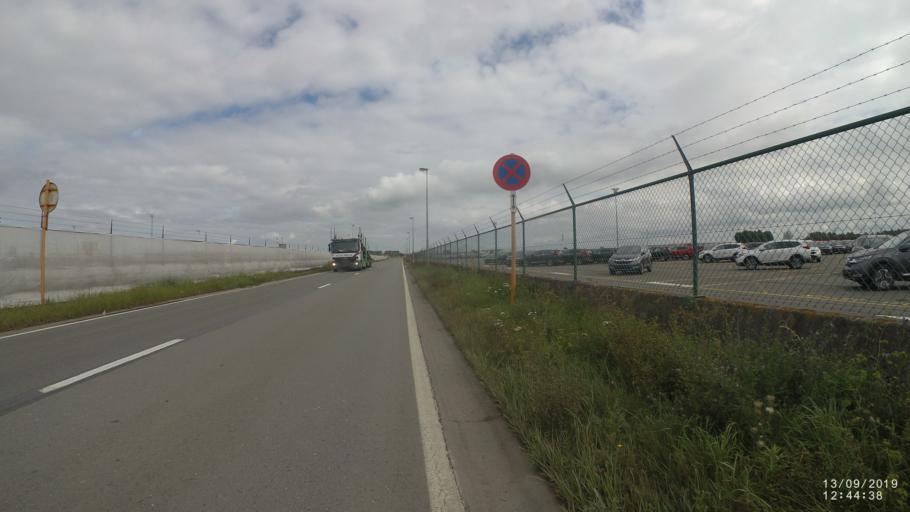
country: BE
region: Flanders
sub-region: Provincie Oost-Vlaanderen
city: Evergem
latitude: 51.1103
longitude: 3.7601
